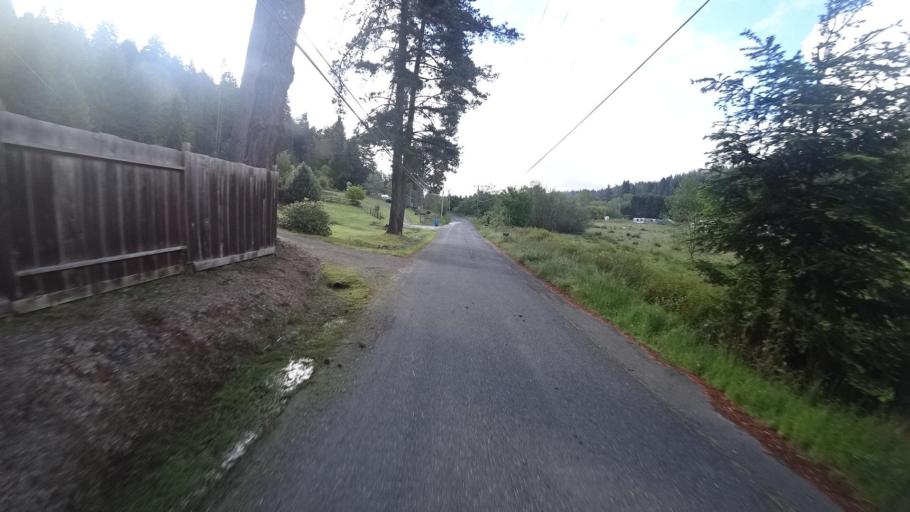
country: US
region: California
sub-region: Humboldt County
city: Arcata
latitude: 40.8875
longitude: -124.0365
